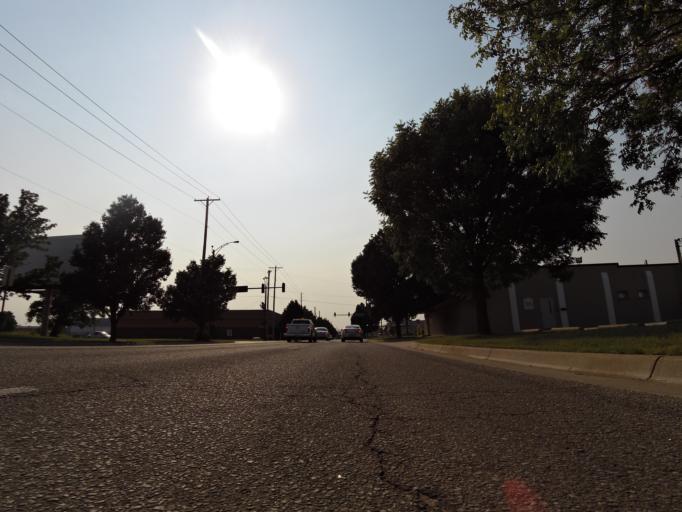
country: US
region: Kansas
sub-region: Sedgwick County
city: Wichita
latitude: 37.6976
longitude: -97.3258
